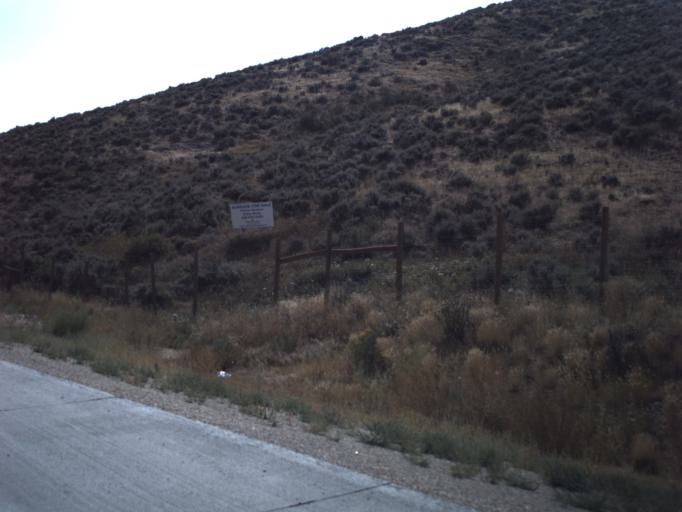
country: US
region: Utah
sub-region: Summit County
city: Snyderville
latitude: 40.7492
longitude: -111.4718
